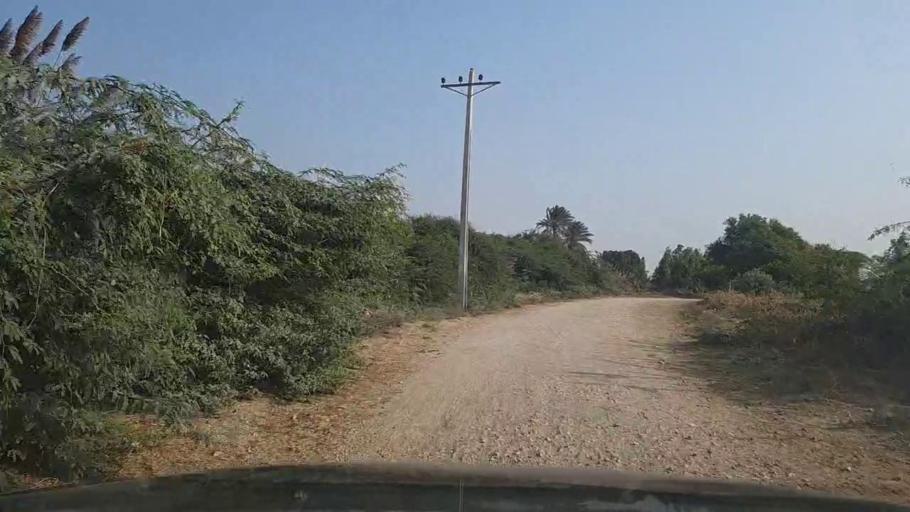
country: PK
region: Sindh
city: Mirpur Sakro
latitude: 24.6336
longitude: 67.7557
